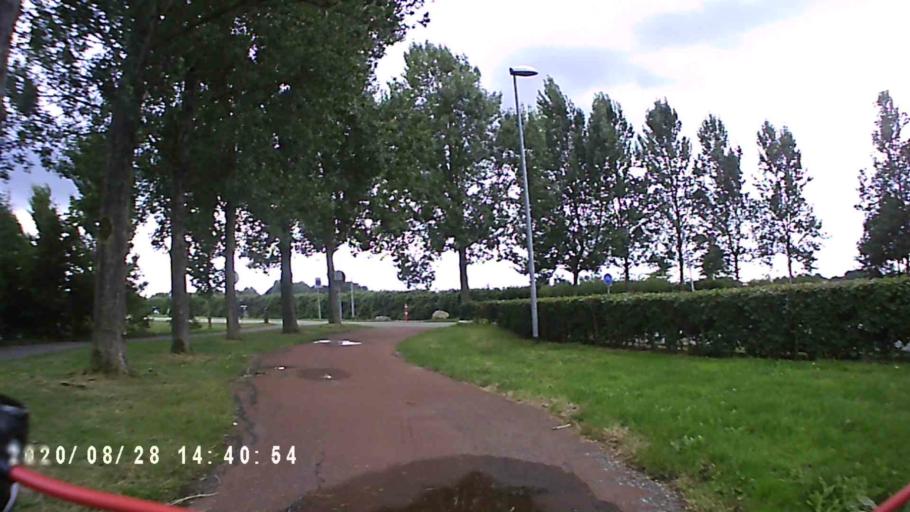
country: NL
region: Groningen
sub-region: Gemeente Groningen
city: Groningen
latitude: 53.1804
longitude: 6.5528
